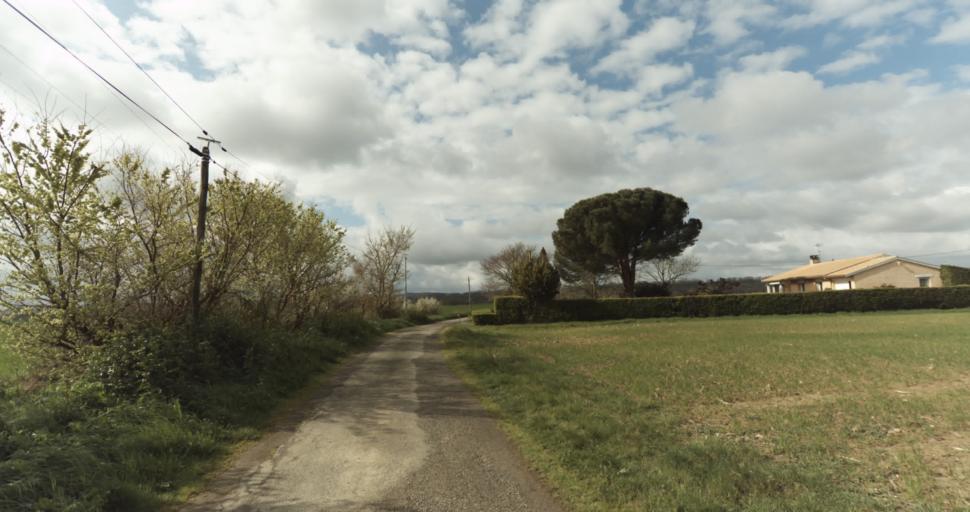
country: FR
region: Midi-Pyrenees
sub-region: Departement de la Haute-Garonne
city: Miremont
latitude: 43.3602
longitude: 1.4415
